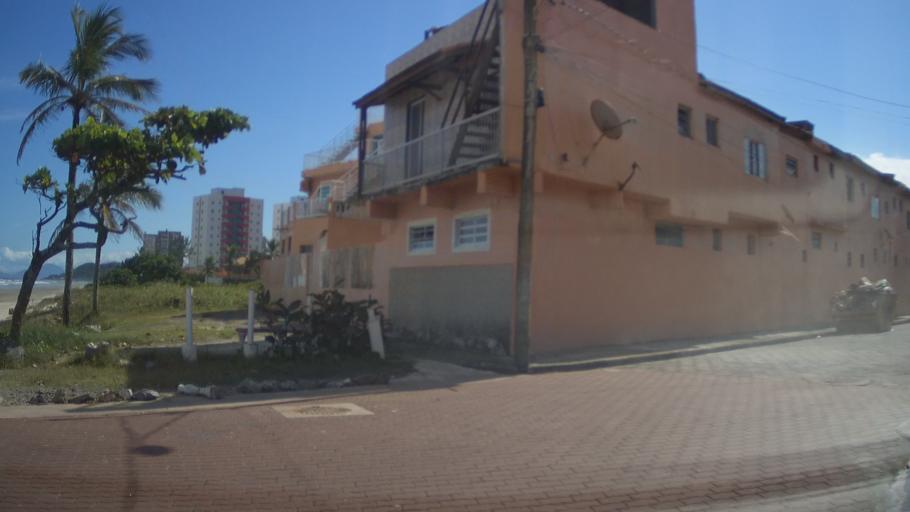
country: BR
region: Sao Paulo
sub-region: Itanhaem
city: Itanhaem
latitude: -24.1785
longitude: -46.7730
